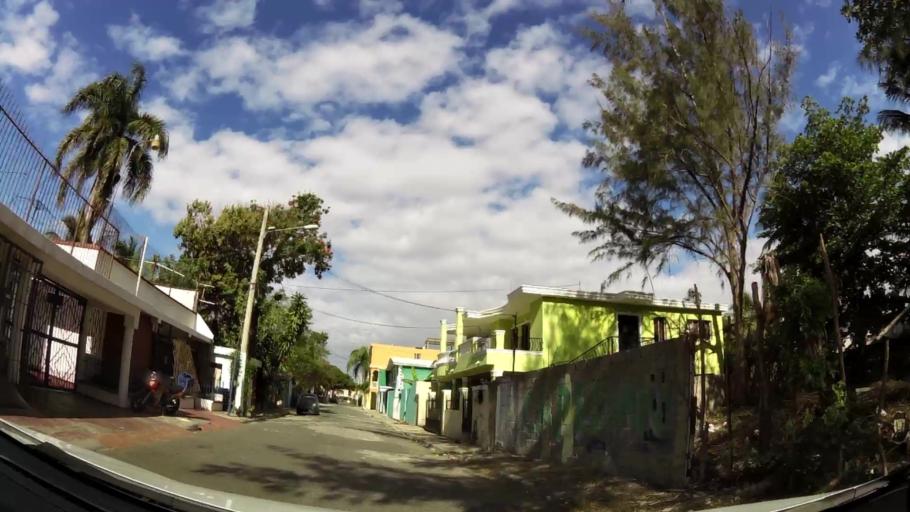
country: DO
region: Santo Domingo
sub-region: Santo Domingo
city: Boca Chica
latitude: 18.4540
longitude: -69.6066
